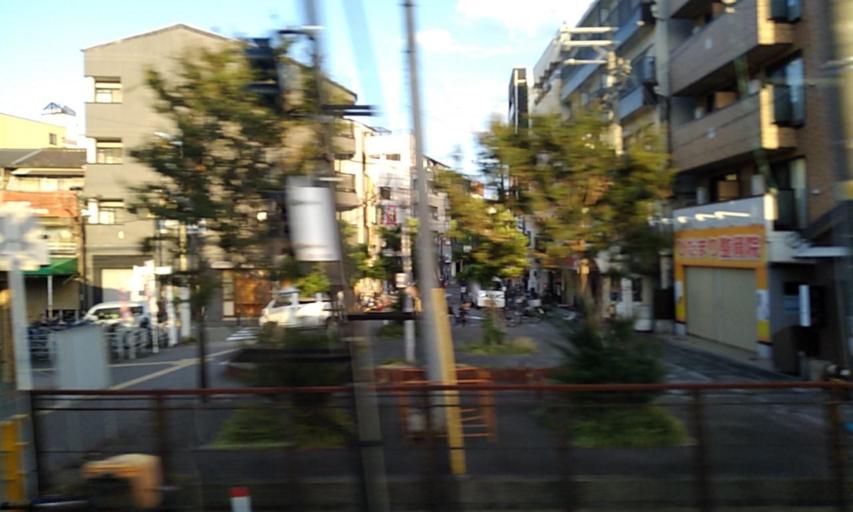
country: JP
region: Osaka
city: Sakai
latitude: 34.6057
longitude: 135.4970
